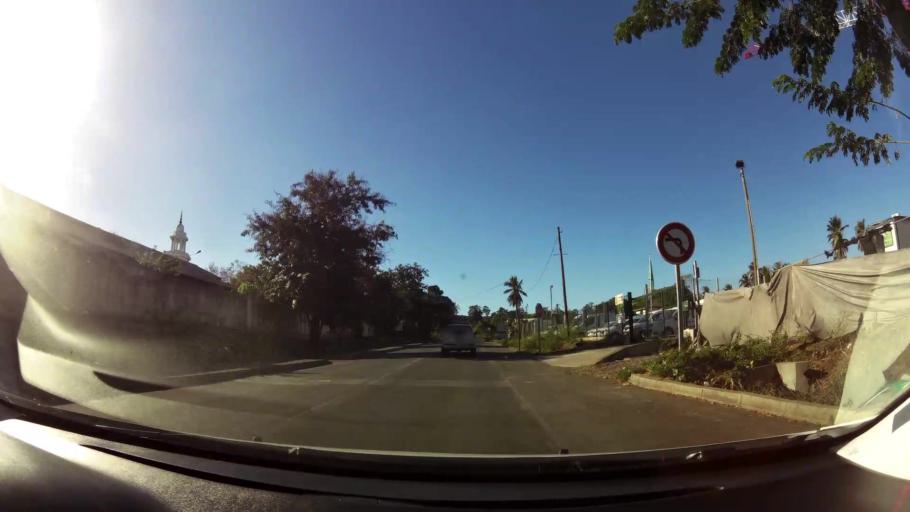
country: YT
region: Mamoudzou
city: Mamoudzou
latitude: -12.7647
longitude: 45.2254
